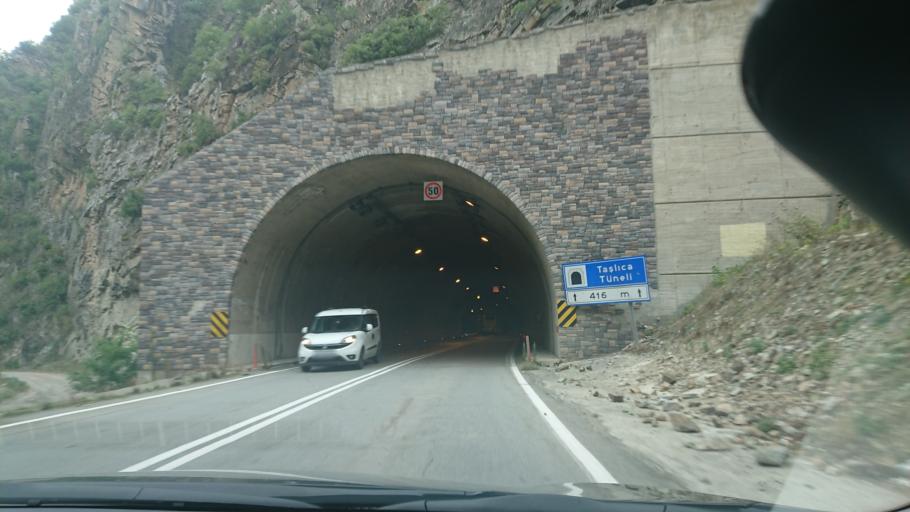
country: TR
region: Gumushane
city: Kurtun
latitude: 40.7078
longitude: 39.0650
